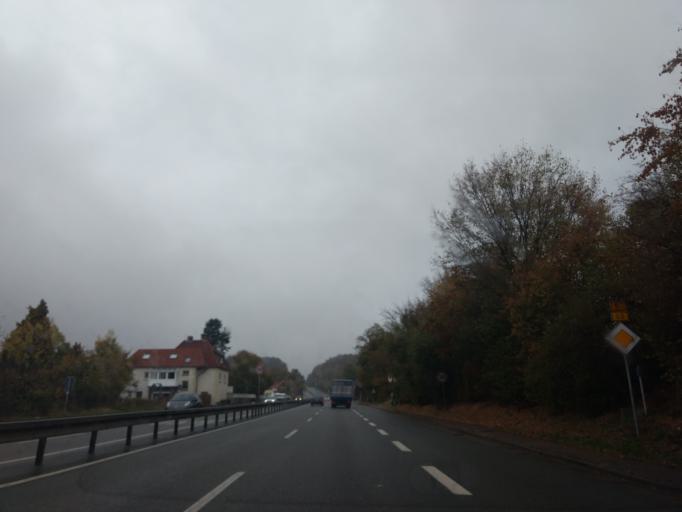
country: DE
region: Lower Saxony
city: Georgsmarienhutte
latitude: 52.2271
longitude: 8.0660
